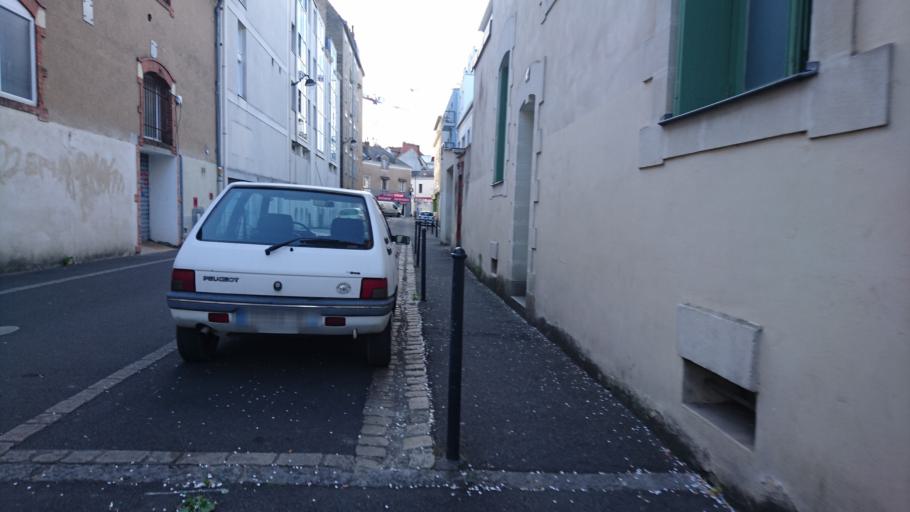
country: FR
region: Pays de la Loire
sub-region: Departement de la Loire-Atlantique
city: Nantes
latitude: 47.2128
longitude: -1.5473
